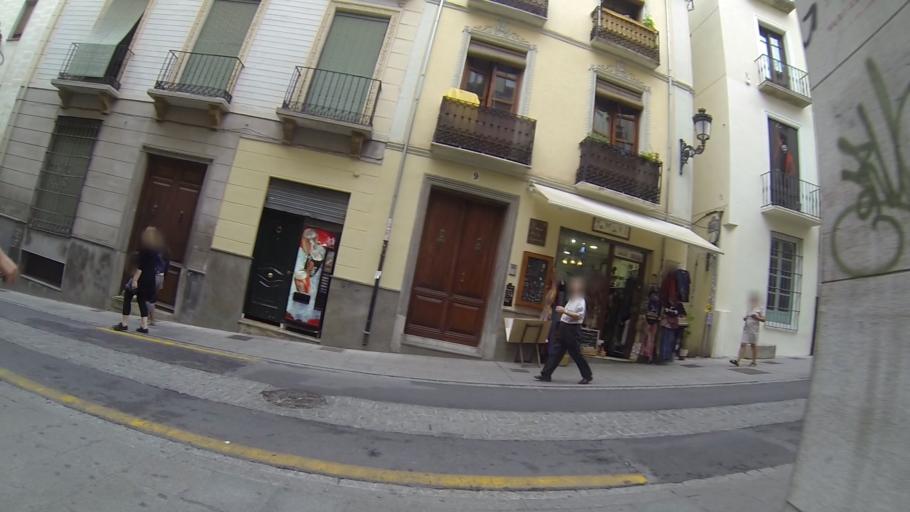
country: ES
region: Andalusia
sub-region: Provincia de Granada
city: Granada
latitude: 37.1763
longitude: -3.5954
